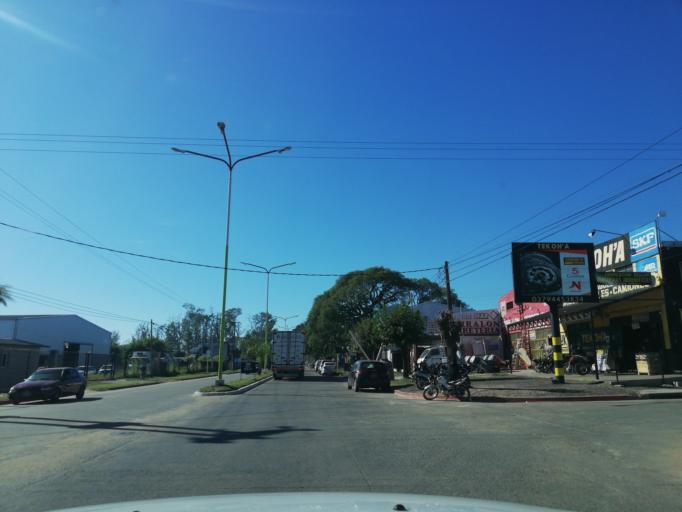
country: AR
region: Corrientes
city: Corrientes
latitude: -27.4761
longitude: -58.7926
